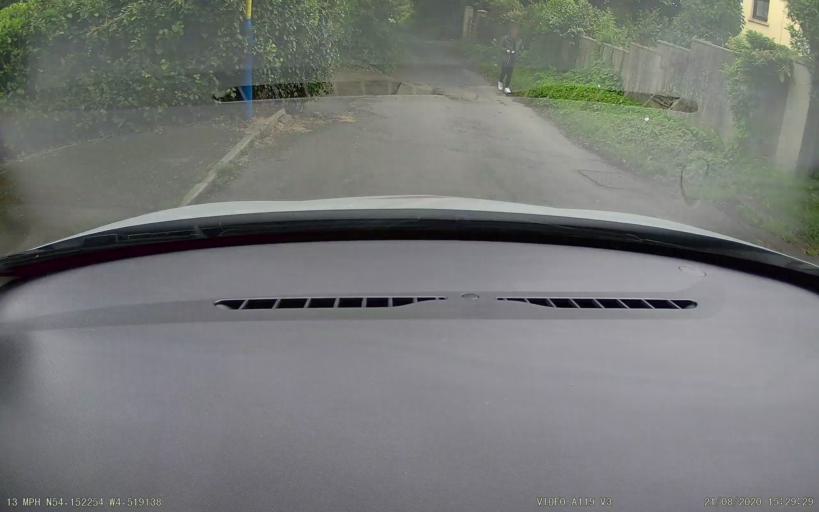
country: IM
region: Douglas
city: Douglas
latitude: 54.1523
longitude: -4.5191
